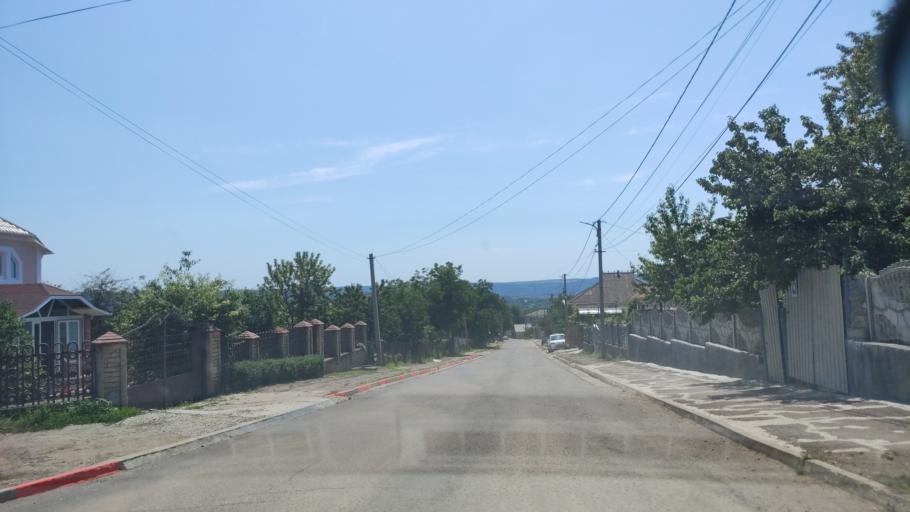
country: MD
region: Raionul Soroca
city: Soroca
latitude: 48.1705
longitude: 28.2981
